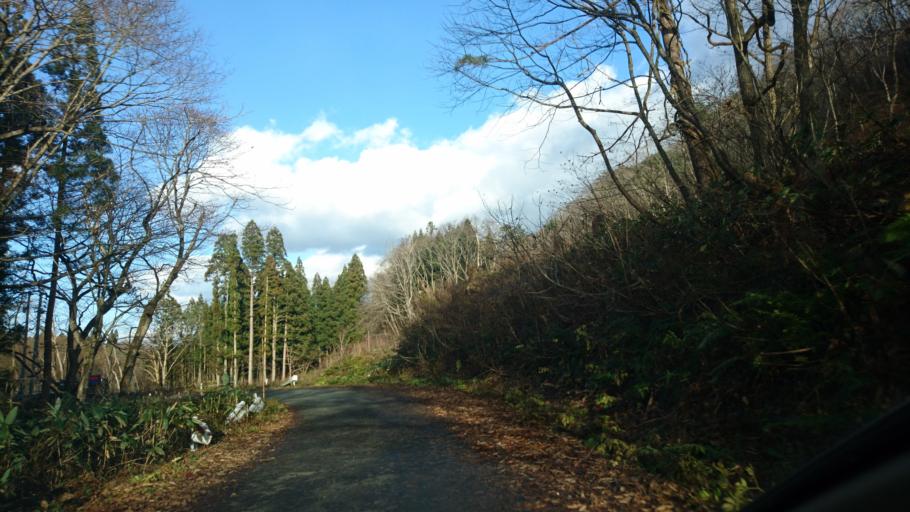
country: JP
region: Akita
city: Kakunodatemachi
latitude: 39.4806
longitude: 140.8073
